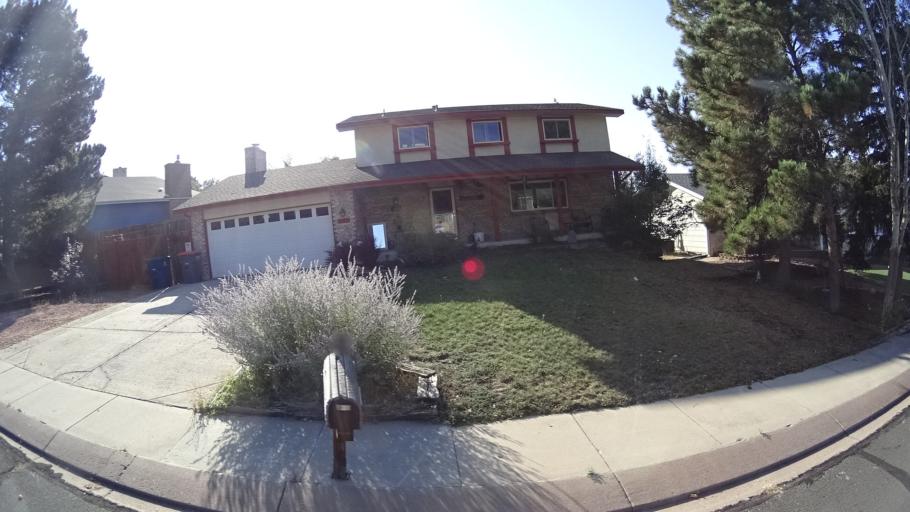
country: US
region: Colorado
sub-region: El Paso County
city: Cimarron Hills
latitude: 38.8893
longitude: -104.7294
